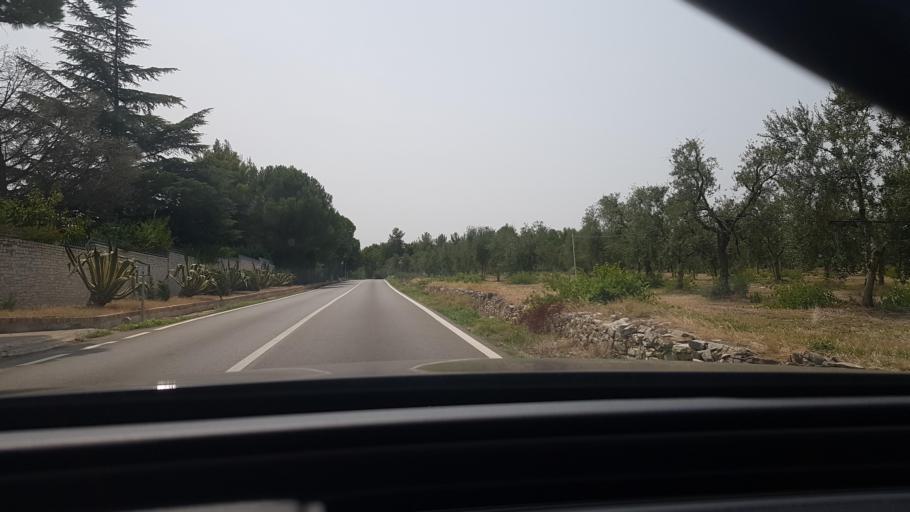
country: IT
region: Apulia
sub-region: Provincia di Barletta - Andria - Trani
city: Andria
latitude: 41.1439
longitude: 16.2896
